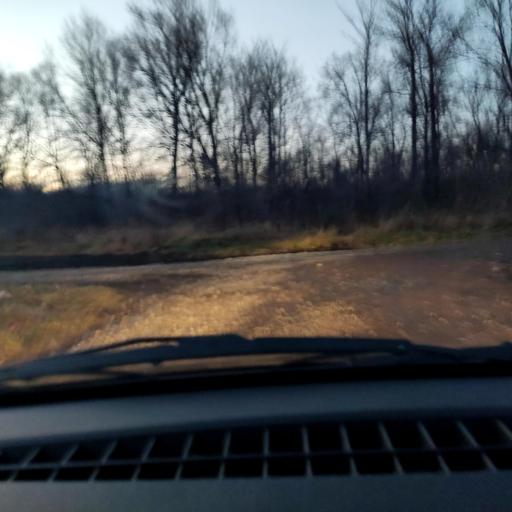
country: RU
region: Bashkortostan
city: Ufa
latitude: 54.6556
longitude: 55.8865
